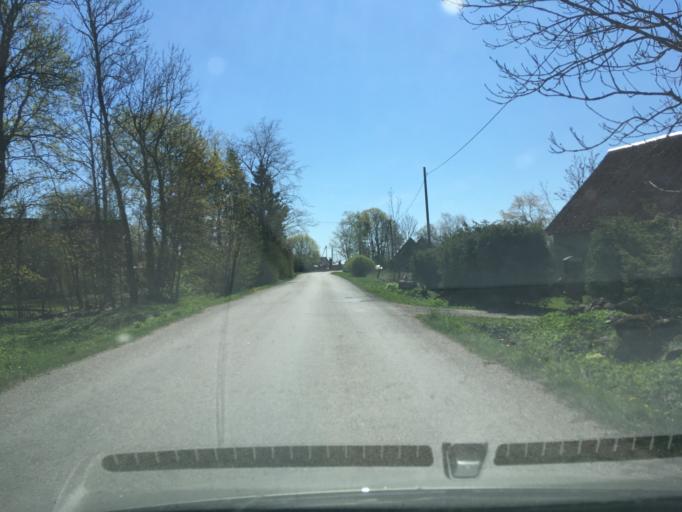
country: EE
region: Harju
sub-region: Raasiku vald
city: Arukula
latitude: 59.3913
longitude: 25.0802
